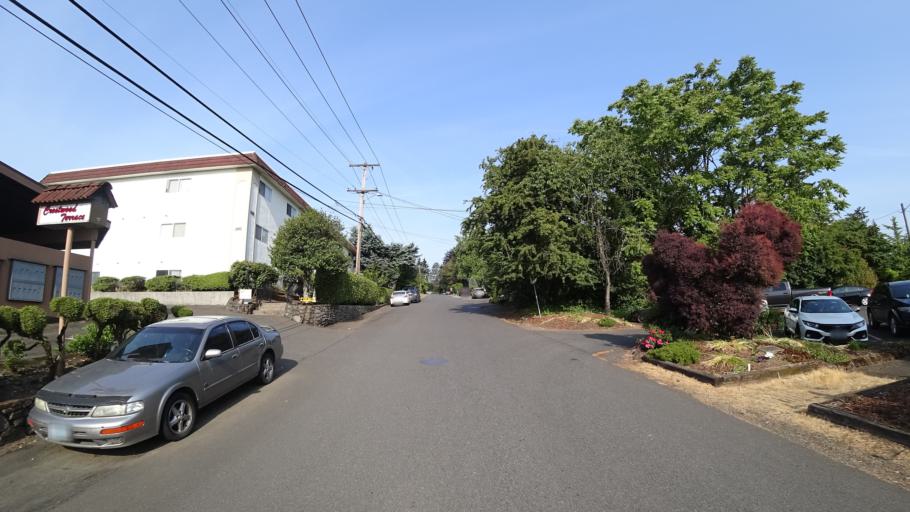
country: US
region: Oregon
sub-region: Washington County
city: Garden Home-Whitford
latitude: 45.4584
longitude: -122.7116
